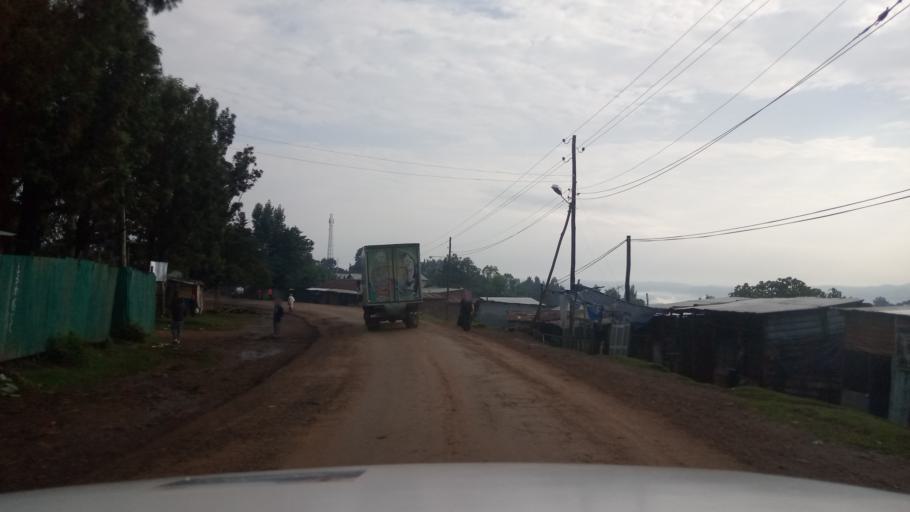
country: ET
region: Oromiya
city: Agaro
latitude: 7.7877
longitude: 36.7276
